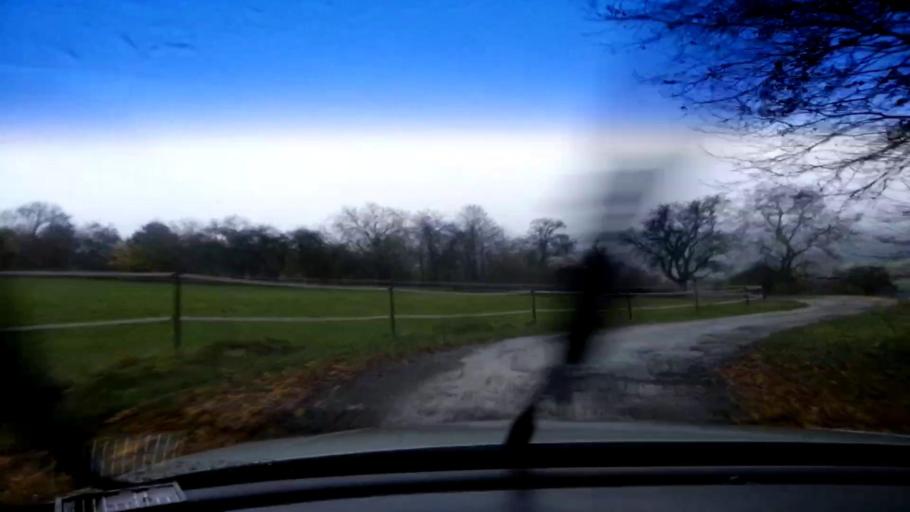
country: DE
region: Bavaria
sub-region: Upper Franconia
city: Schesslitz
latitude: 49.9546
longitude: 11.0351
